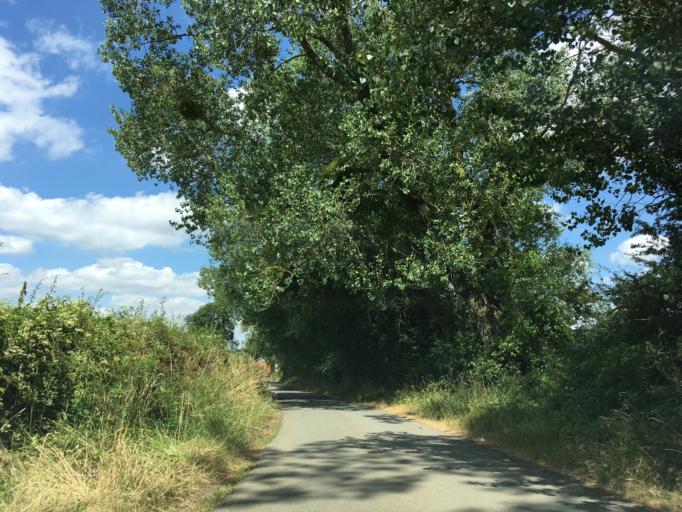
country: GB
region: England
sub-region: Gloucestershire
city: Shurdington
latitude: 51.8506
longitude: -2.1349
